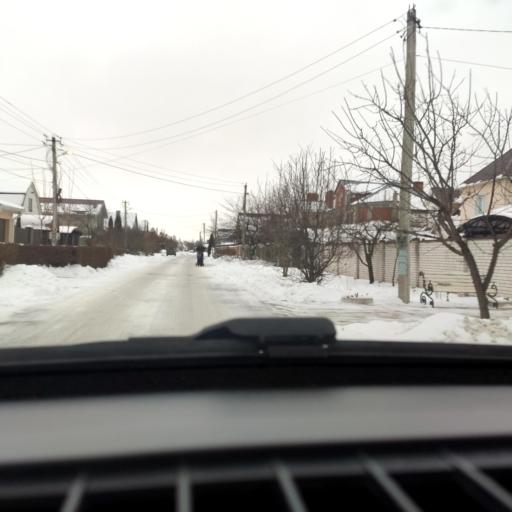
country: RU
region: Voronezj
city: Somovo
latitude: 51.6874
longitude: 39.3097
